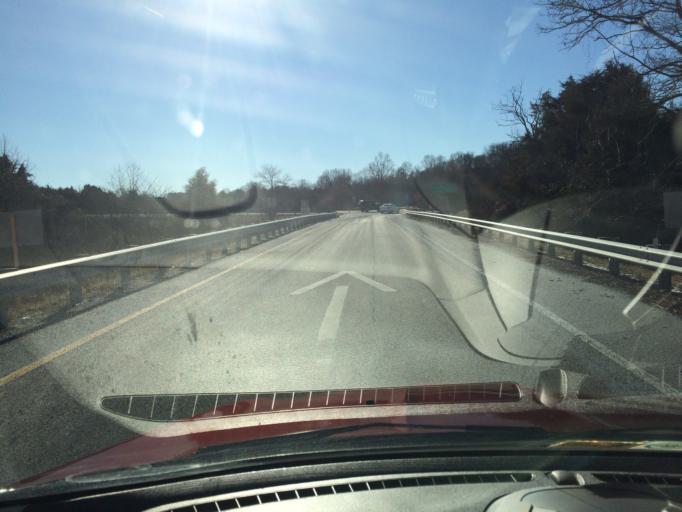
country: US
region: Virginia
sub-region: Rockbridge County
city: East Lexington
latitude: 37.7583
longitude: -79.4103
